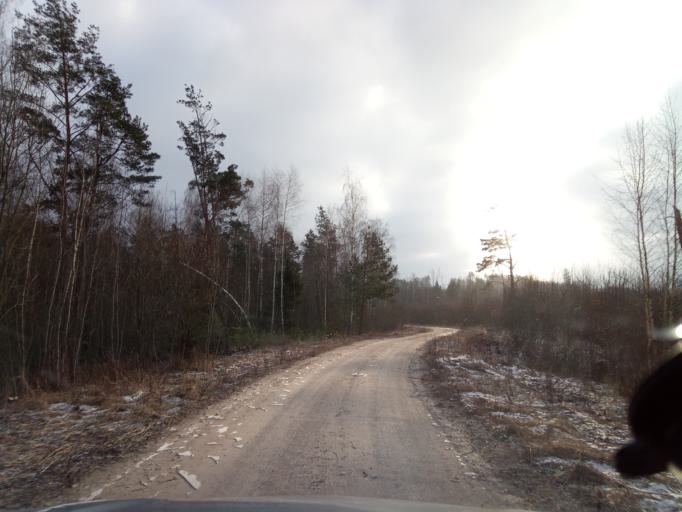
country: LT
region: Alytaus apskritis
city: Varena
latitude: 54.3688
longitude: 24.5457
